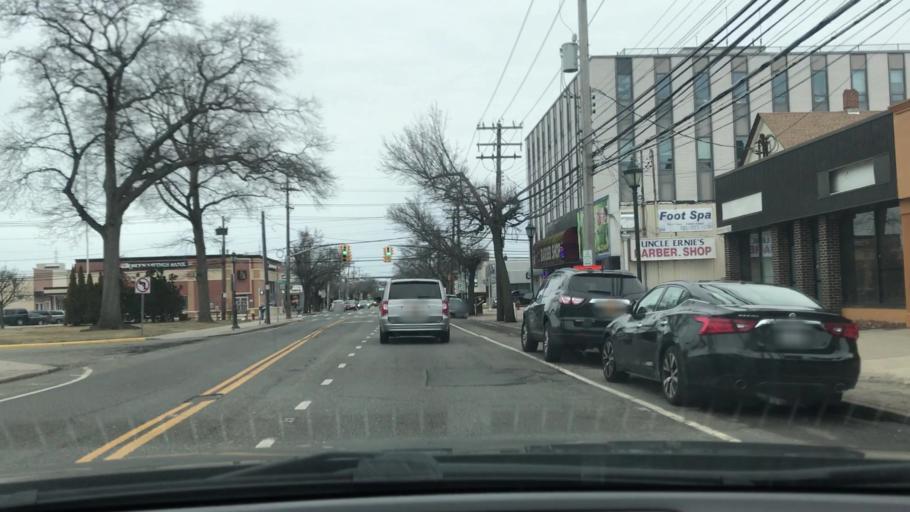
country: US
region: New York
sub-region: Nassau County
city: Merrick
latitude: 40.6670
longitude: -73.5536
